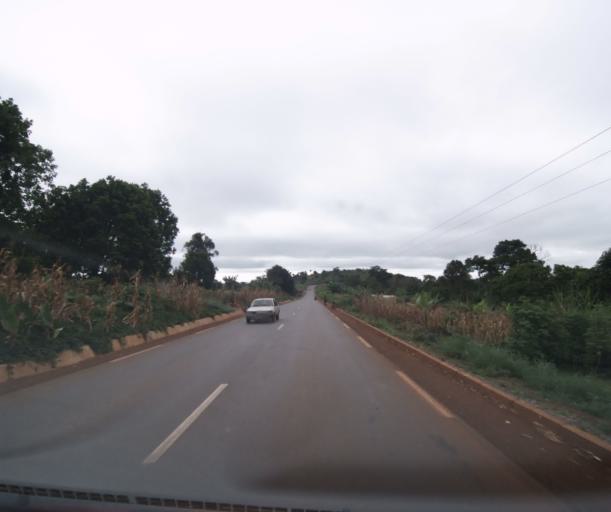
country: CM
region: West
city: Mbouda
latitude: 5.5539
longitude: 10.3220
